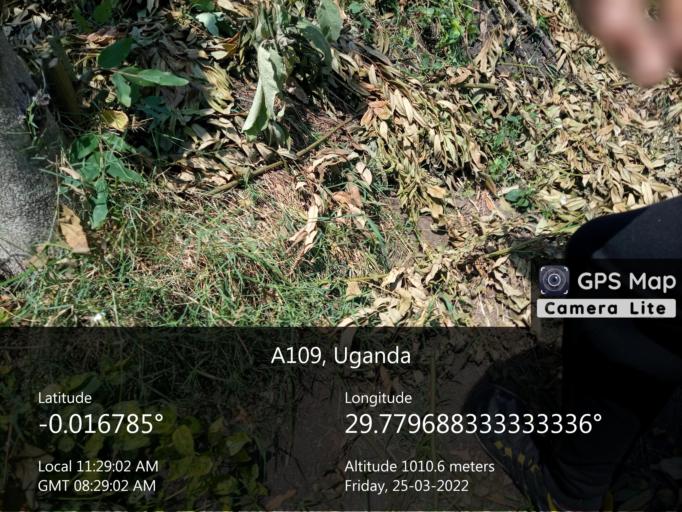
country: UG
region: Western Region
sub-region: Kasese District
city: Kilembe
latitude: -0.0168
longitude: 29.7797
